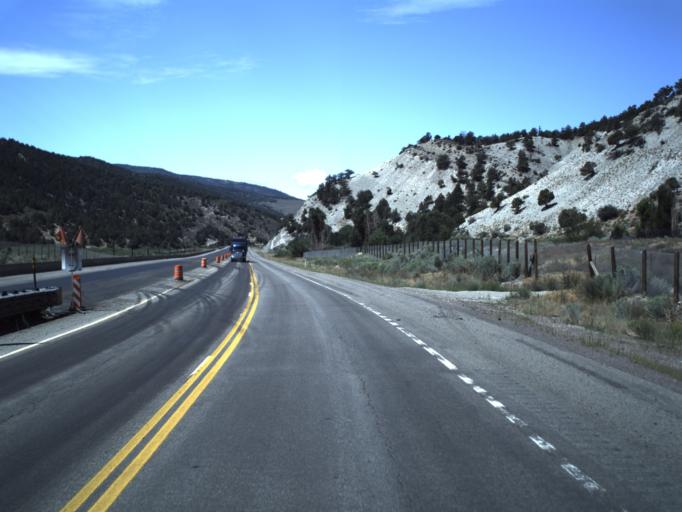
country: US
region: Utah
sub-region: Utah County
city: Mapleton
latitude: 39.9568
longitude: -111.2496
